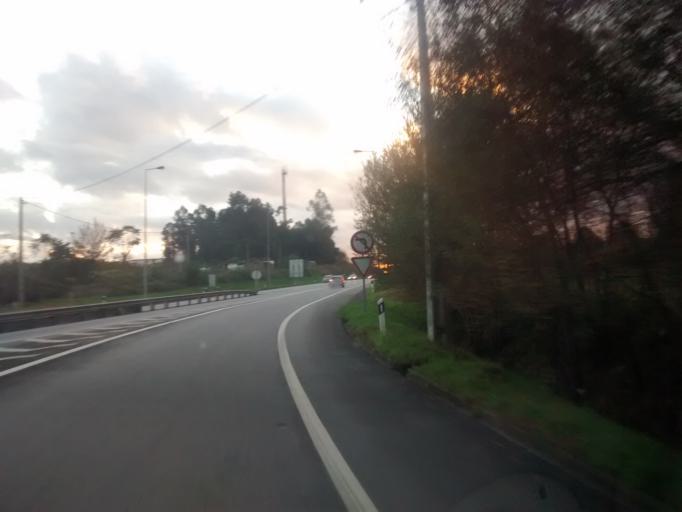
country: PT
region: Braga
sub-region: Vila Verde
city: Prado
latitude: 41.6064
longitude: -8.4599
